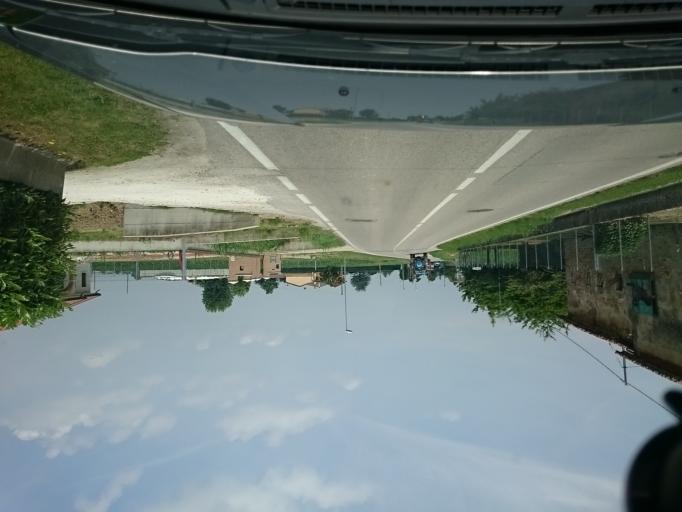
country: IT
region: Veneto
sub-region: Provincia di Padova
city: Brugine
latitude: 45.3151
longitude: 11.9909
